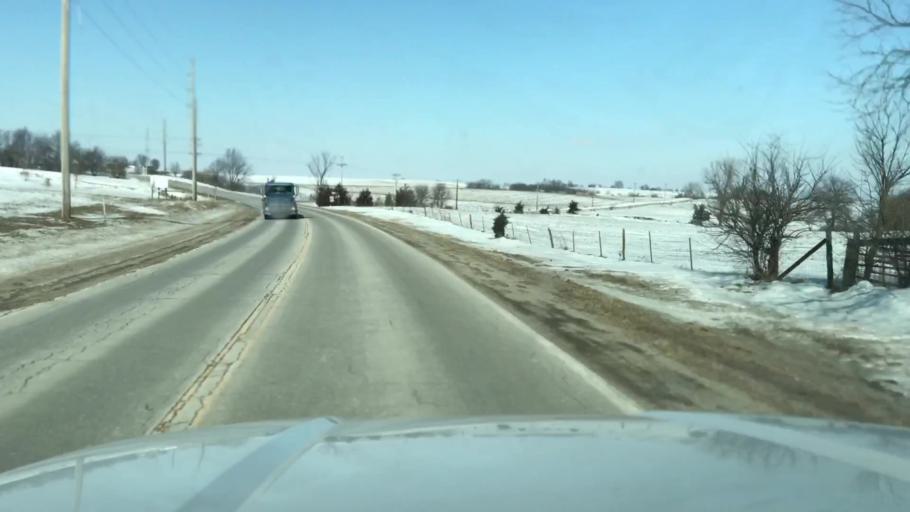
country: US
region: Missouri
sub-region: Andrew County
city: Savannah
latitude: 39.9572
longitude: -94.8502
